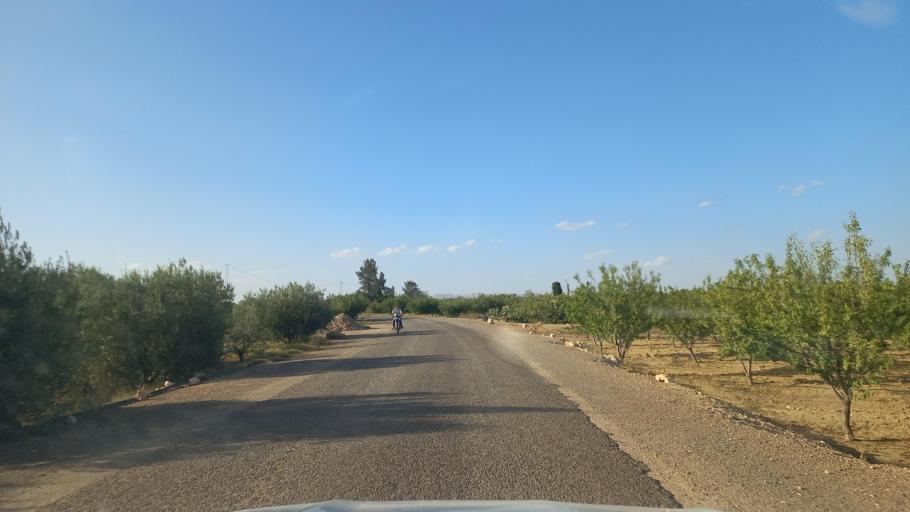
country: TN
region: Al Qasrayn
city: Kasserine
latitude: 35.2643
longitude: 9.0283
